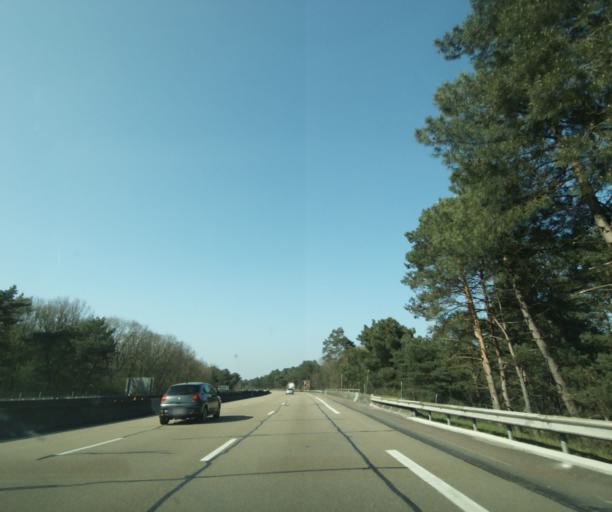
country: FR
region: Ile-de-France
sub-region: Departement de Seine-et-Marne
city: Acheres-la-Foret
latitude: 48.3760
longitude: 2.5619
